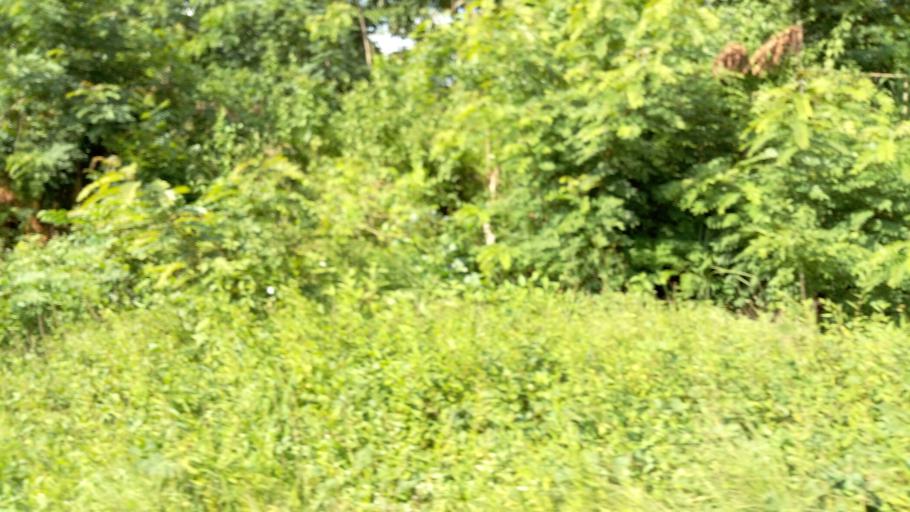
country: TG
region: Plateaux
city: Kpalime
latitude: 6.8464
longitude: 0.5788
